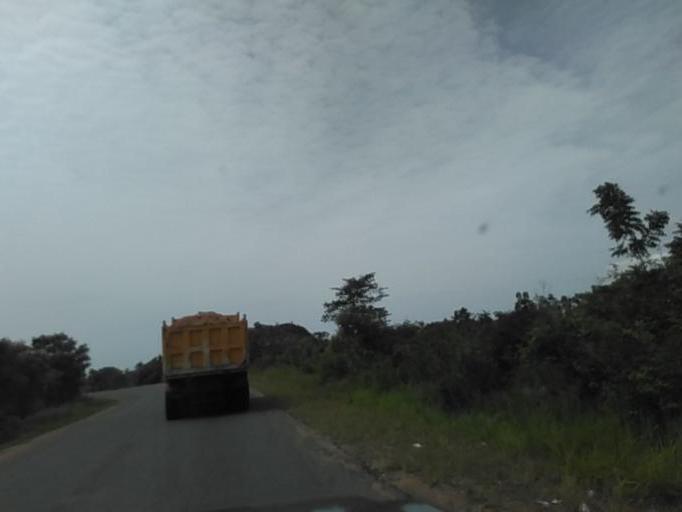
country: GH
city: Akropong
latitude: 6.0939
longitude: 0.0614
